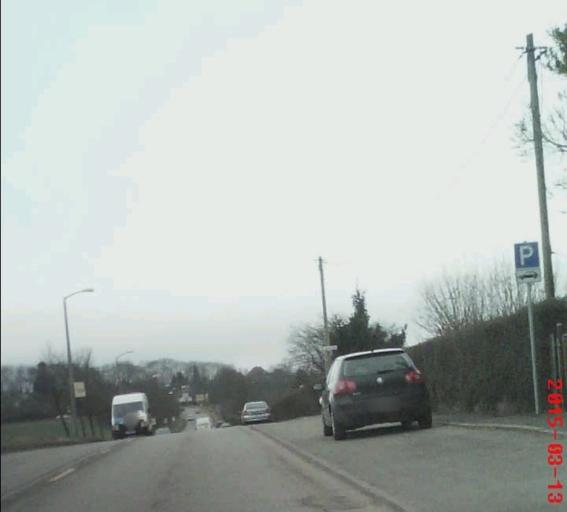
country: DE
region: Thuringia
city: Bad Langensalza
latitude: 51.1175
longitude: 10.6591
